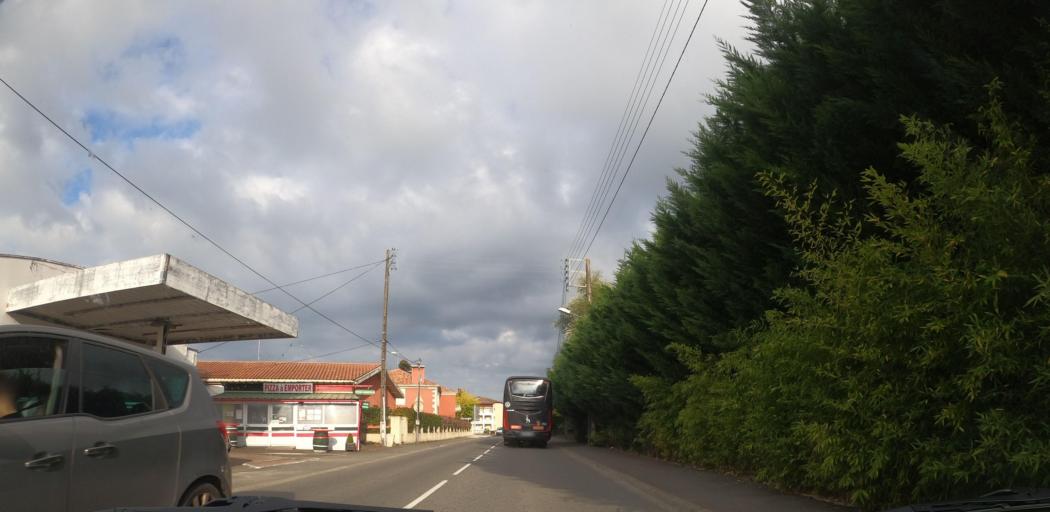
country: FR
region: Aquitaine
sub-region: Departement des Landes
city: Soustons
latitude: 43.7527
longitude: -1.3245
